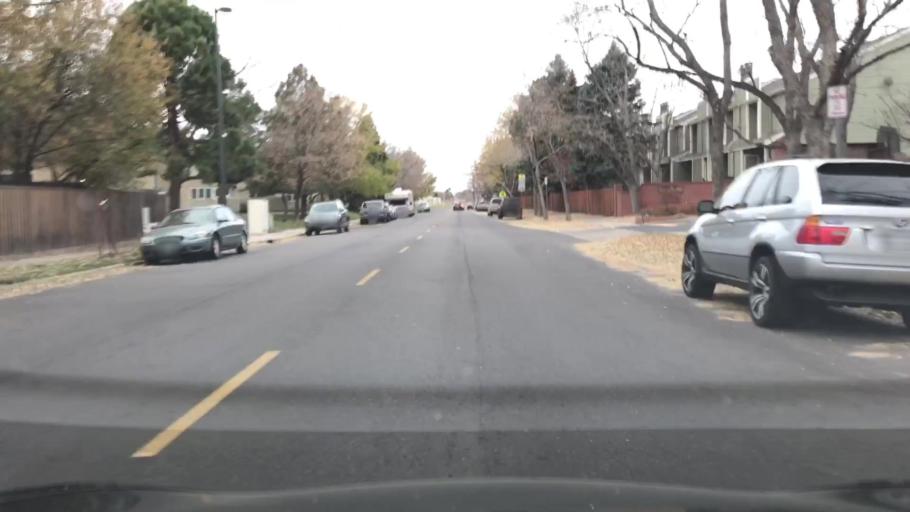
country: US
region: Colorado
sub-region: Arapahoe County
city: Glendale
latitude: 39.6893
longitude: -104.9007
